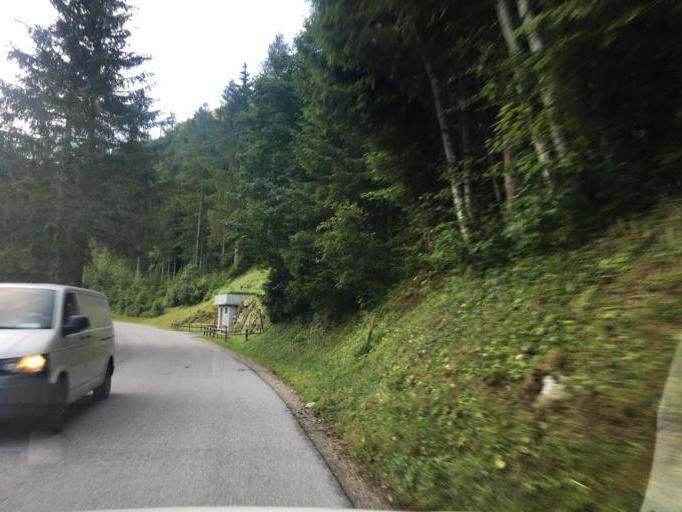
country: AT
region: Styria
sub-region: Politischer Bezirk Liezen
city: Schladming
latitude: 47.3578
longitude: 13.6928
